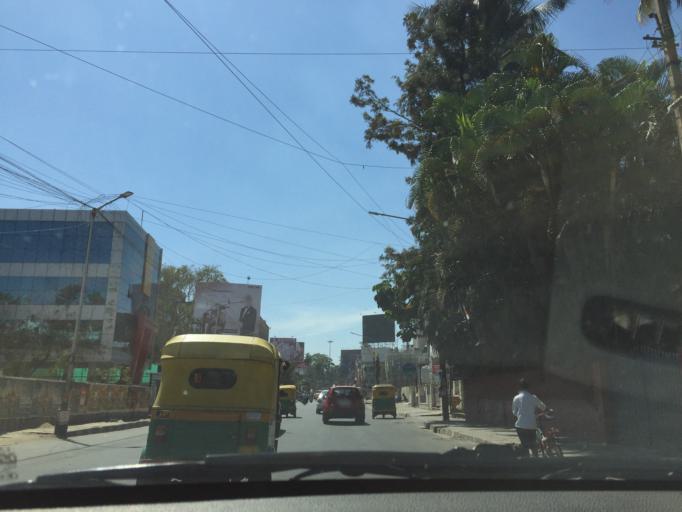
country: IN
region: Karnataka
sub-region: Bangalore Urban
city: Bangalore
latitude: 12.9573
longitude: 77.5861
